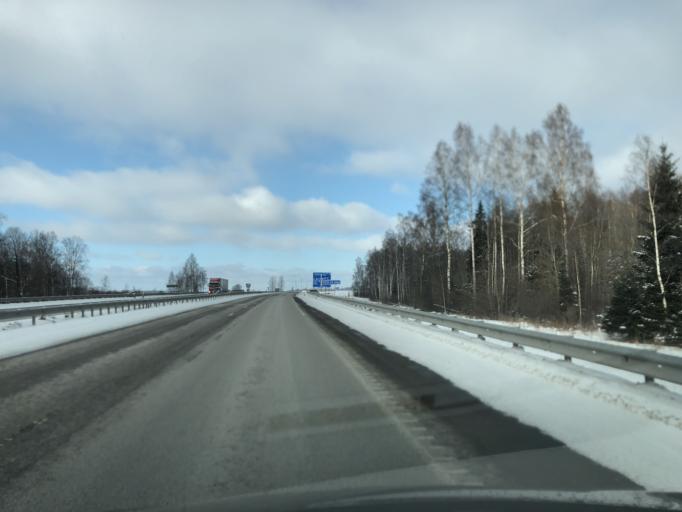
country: EE
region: Jaervamaa
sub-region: Paide linn
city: Paide
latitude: 58.9092
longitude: 25.6274
